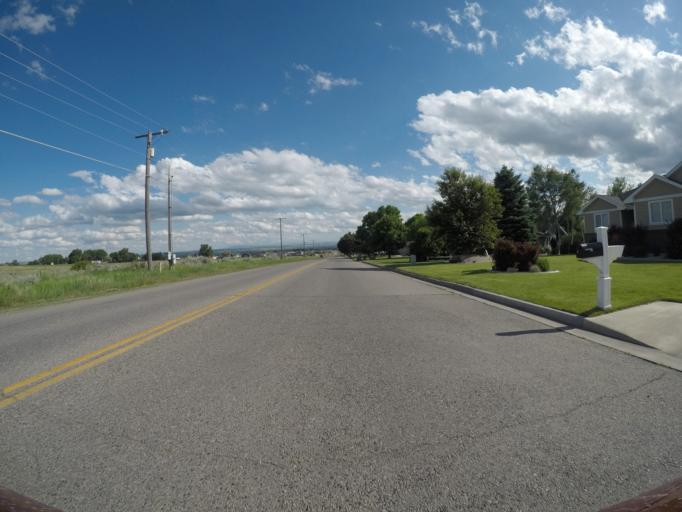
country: US
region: Montana
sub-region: Yellowstone County
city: Billings
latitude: 45.8018
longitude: -108.6527
